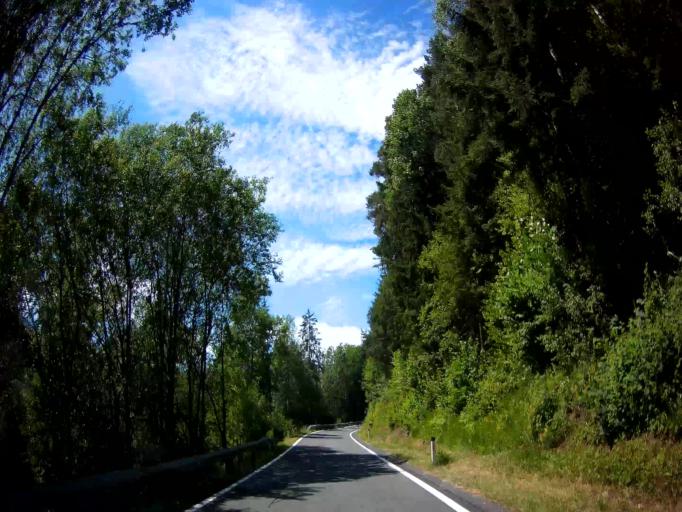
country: AT
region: Carinthia
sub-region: Politischer Bezirk Sankt Veit an der Glan
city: Glodnitz
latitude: 46.9034
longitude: 14.1025
